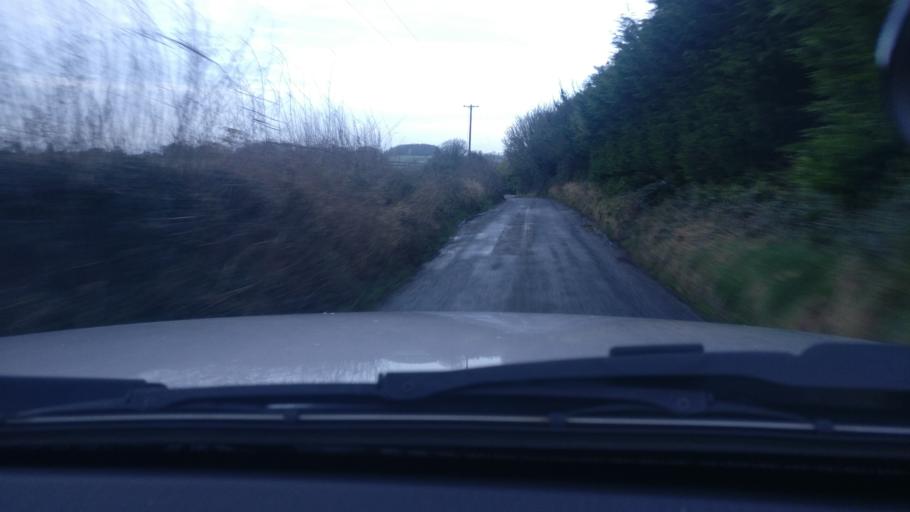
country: IE
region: Connaught
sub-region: County Galway
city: Loughrea
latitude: 53.1685
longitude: -8.5081
